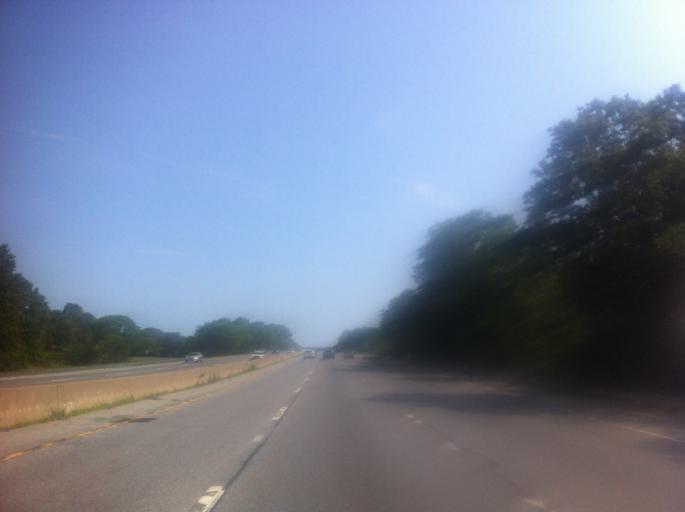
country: US
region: New York
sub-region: Nassau County
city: Plainview
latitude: 40.7616
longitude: -73.4768
